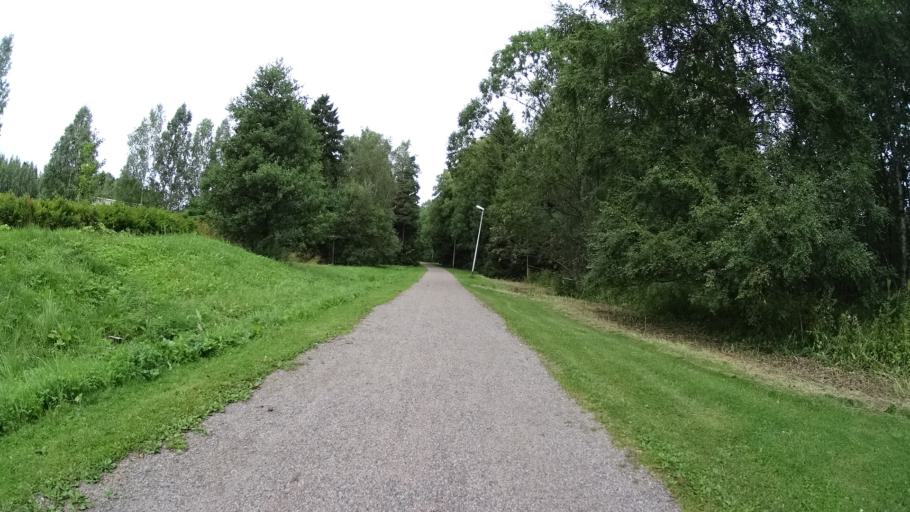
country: FI
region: Uusimaa
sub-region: Helsinki
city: Teekkarikylae
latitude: 60.2661
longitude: 24.8614
